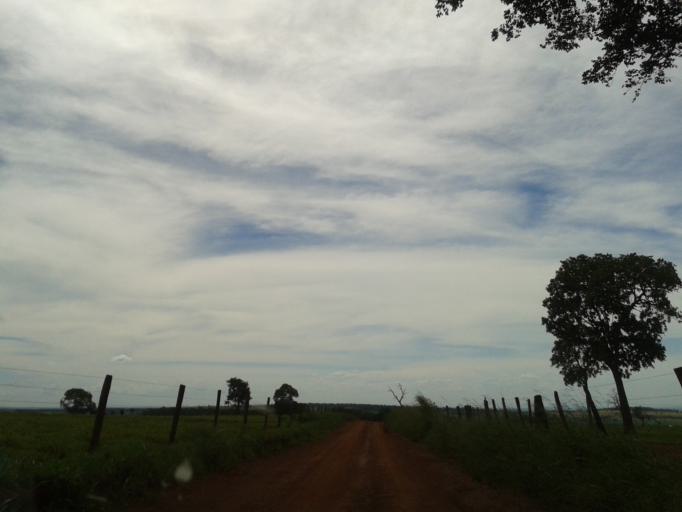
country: BR
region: Minas Gerais
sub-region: Capinopolis
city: Capinopolis
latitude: -18.7502
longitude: -49.8268
